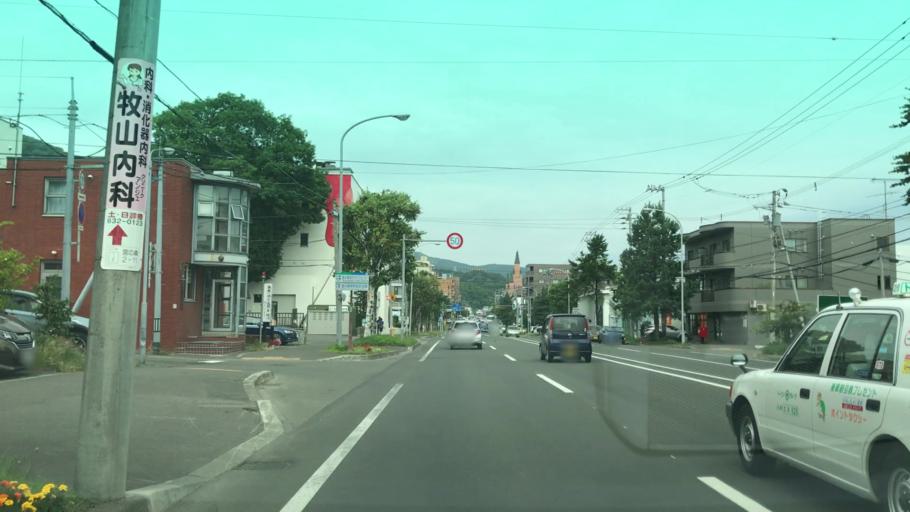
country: JP
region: Hokkaido
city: Sapporo
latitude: 43.0569
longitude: 141.3037
